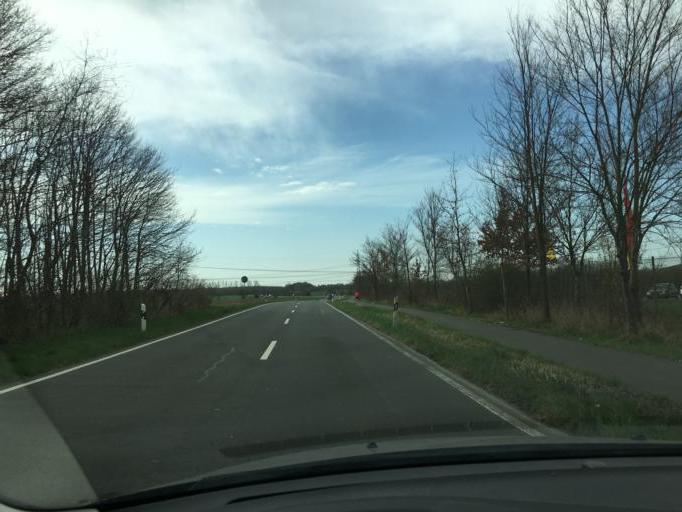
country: DE
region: Saxony
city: Taucha
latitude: 51.3670
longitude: 12.4926
